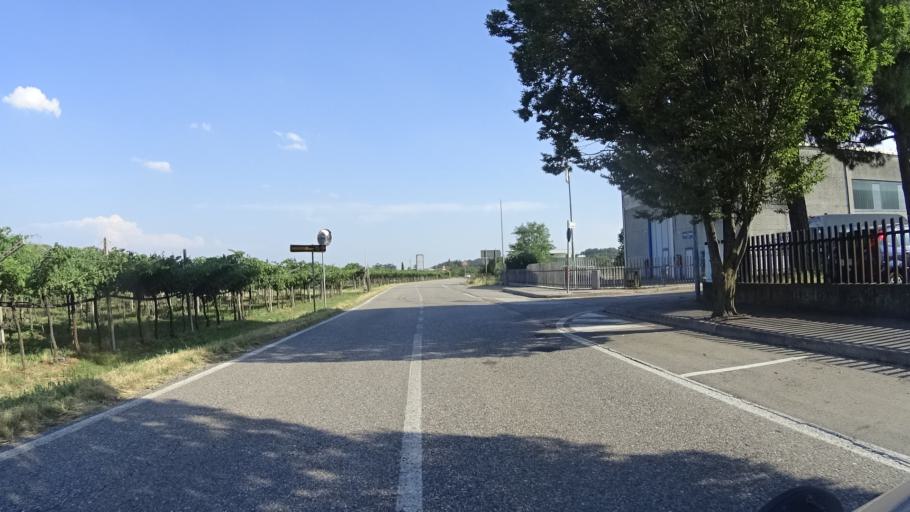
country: IT
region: Veneto
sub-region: Provincia di Verona
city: Calmasino
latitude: 45.5180
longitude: 10.7584
